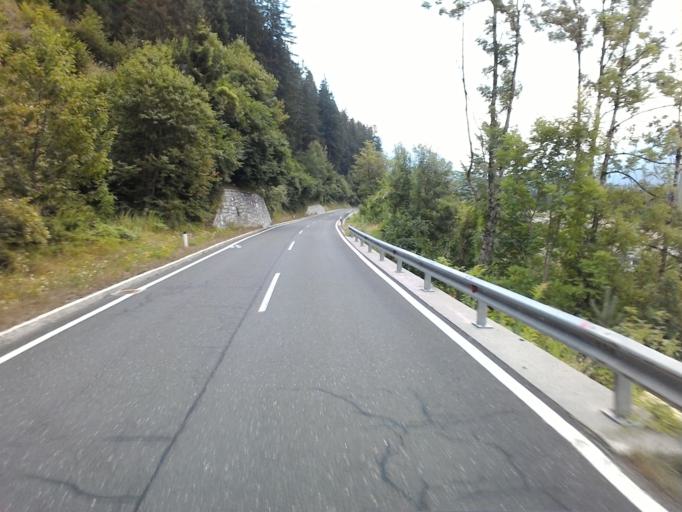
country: AT
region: Carinthia
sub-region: Politischer Bezirk Spittal an der Drau
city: Oberdrauburg
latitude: 46.6700
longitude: 12.9783
